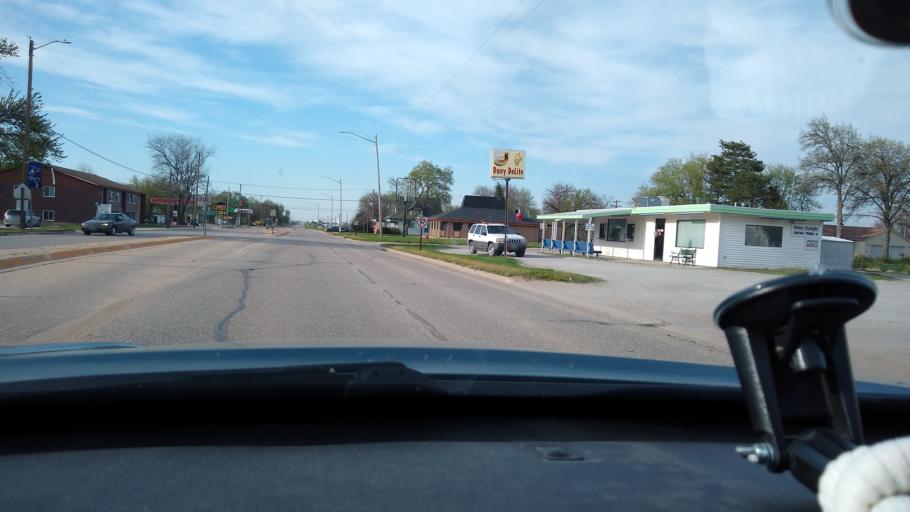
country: US
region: Nebraska
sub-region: Fillmore County
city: Geneva
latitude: 40.5278
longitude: -97.5958
